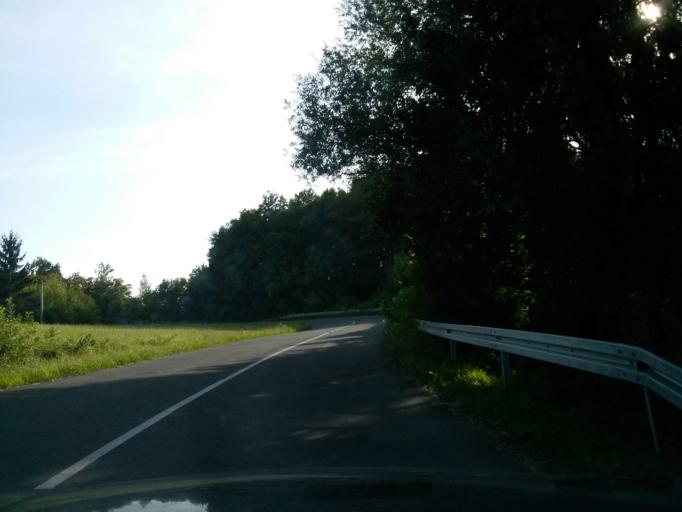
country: HR
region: Sisacko-Moslavacka
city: Gvozd
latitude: 45.5245
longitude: 15.8762
